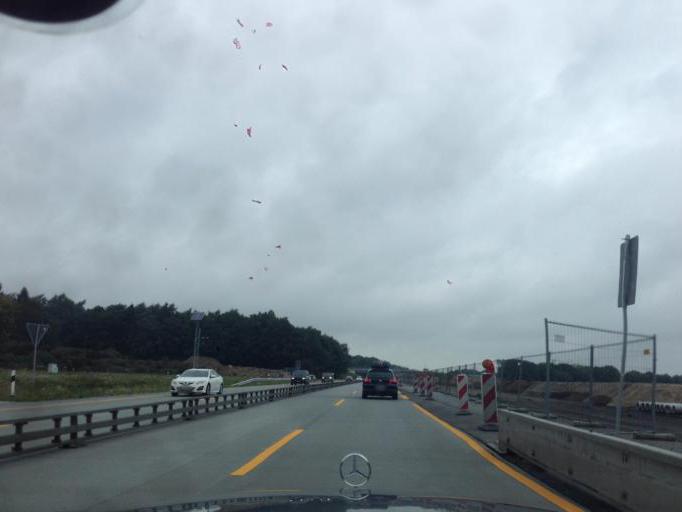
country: DE
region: Schleswig-Holstein
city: Grossenaspe
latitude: 54.0025
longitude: 9.9336
